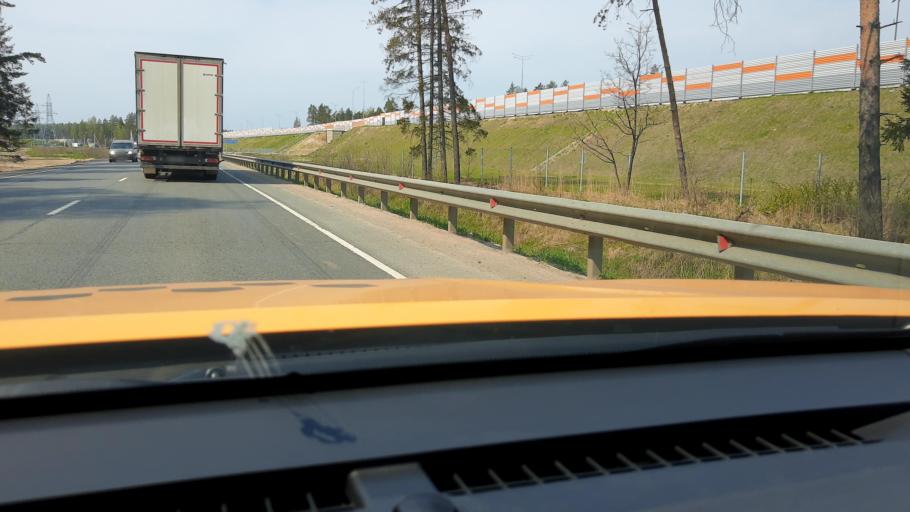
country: RU
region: Moskovskaya
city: Krasnoarmeysk
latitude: 56.0355
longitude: 38.2047
